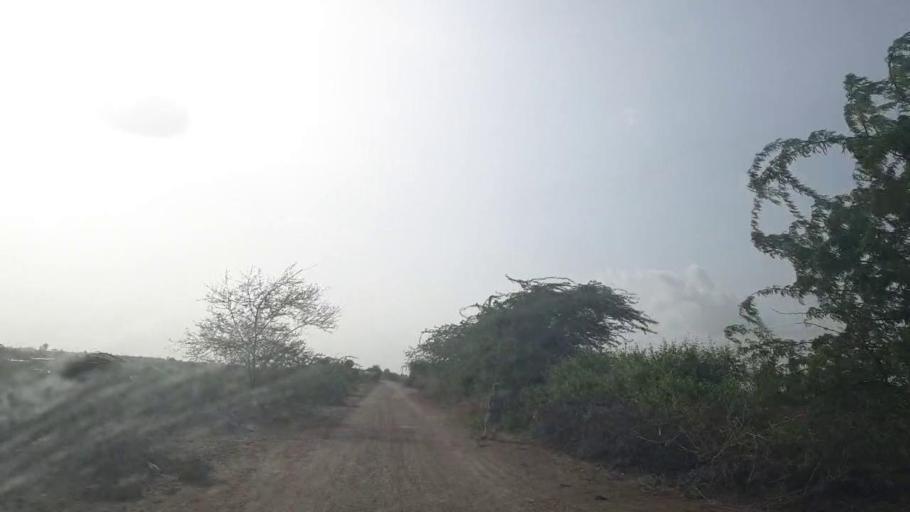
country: PK
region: Sindh
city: Tando Bago
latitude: 24.7634
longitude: 69.0780
